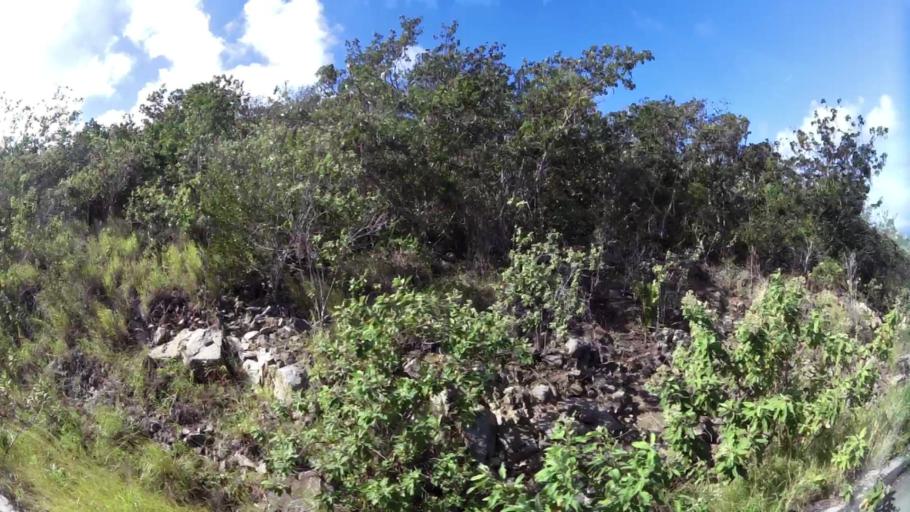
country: VG
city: Tortola
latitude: 18.5004
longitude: -64.4069
